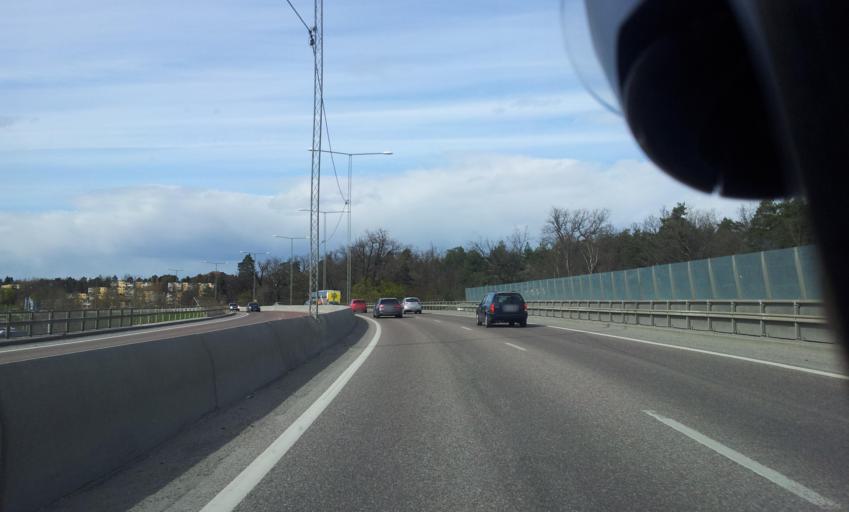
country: SE
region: Stockholm
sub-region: Stockholms Kommun
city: Bromma
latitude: 59.3666
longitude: 17.9446
